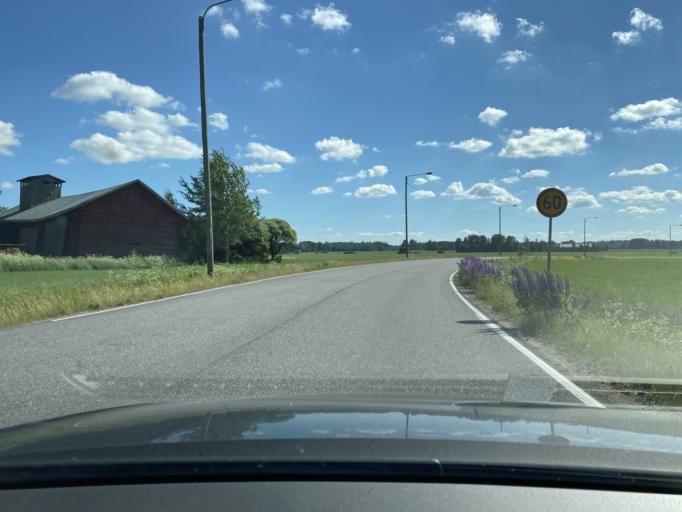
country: FI
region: Satakunta
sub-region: Pori
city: Huittinen
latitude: 61.1658
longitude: 22.7057
